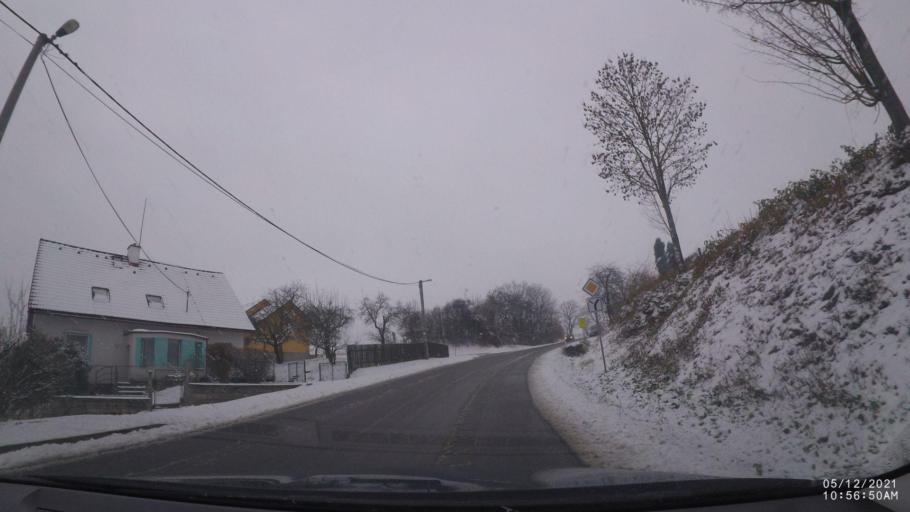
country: CZ
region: Kralovehradecky
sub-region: Okres Rychnov nad Kneznou
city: Rychnov nad Kneznou
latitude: 50.1649
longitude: 16.2672
